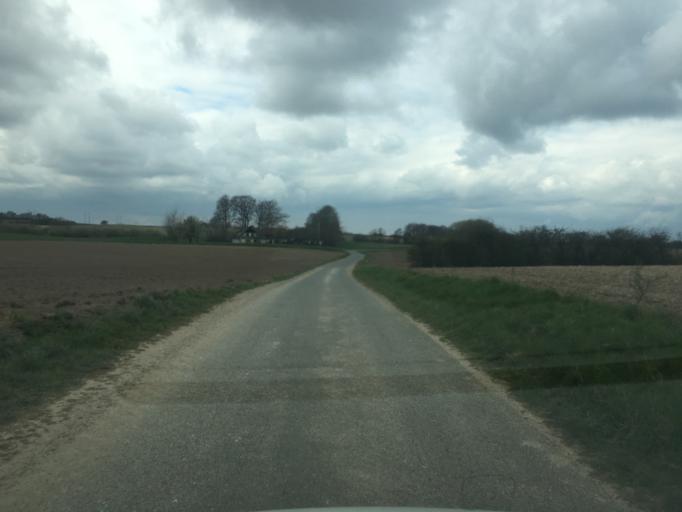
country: DK
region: South Denmark
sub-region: Sonderborg Kommune
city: Grasten
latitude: 55.0054
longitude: 9.5373
